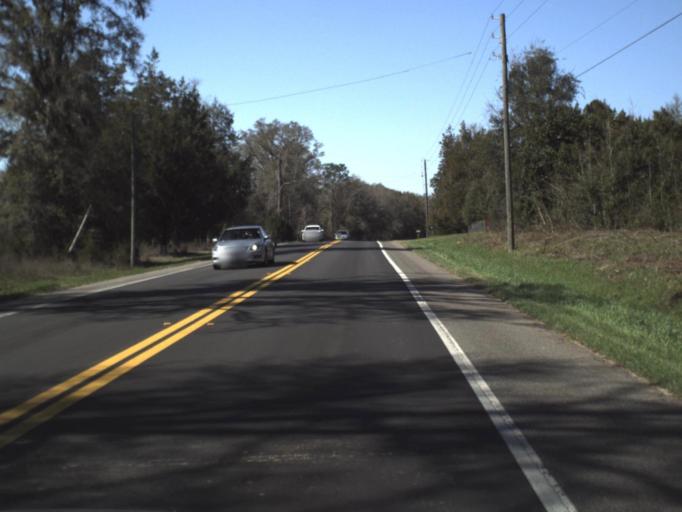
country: US
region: Florida
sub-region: Jackson County
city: Marianna
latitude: 30.6279
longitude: -85.1547
